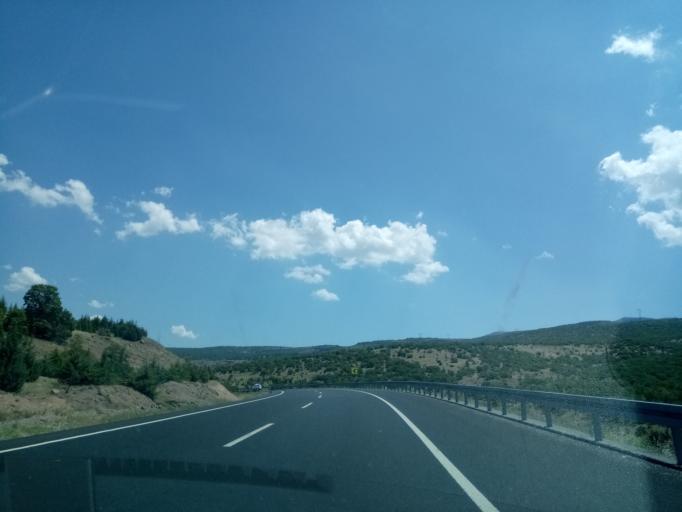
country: TR
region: Konya
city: Cavus
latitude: 37.6390
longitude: 31.9414
